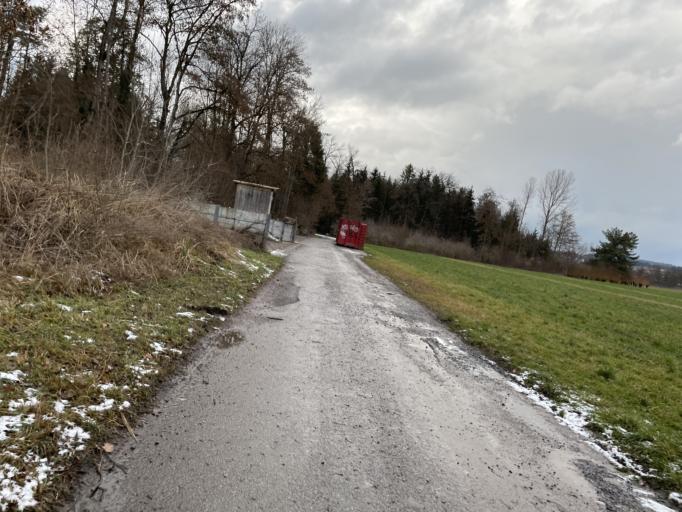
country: CH
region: Bern
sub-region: Bern-Mittelland District
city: Rubigen
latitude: 46.8823
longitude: 7.5463
